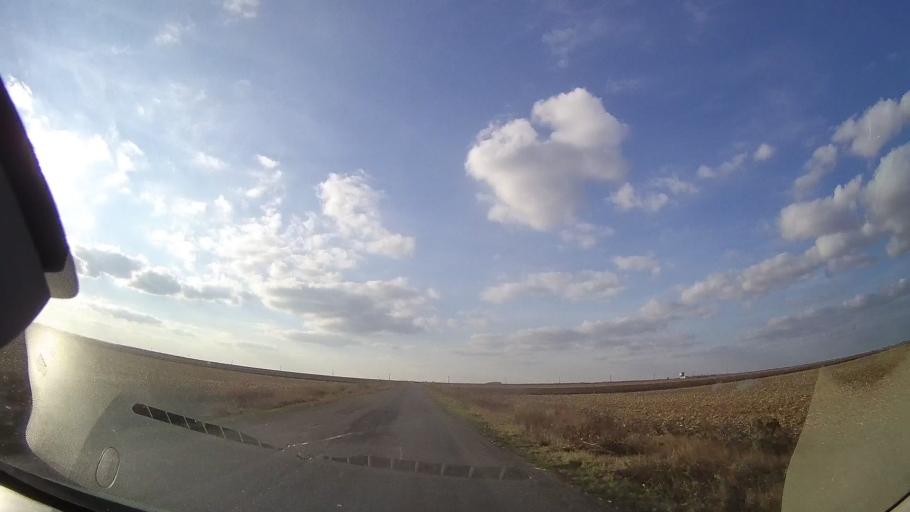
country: RO
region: Constanta
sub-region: Comuna Cerchezu
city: Cerchezu
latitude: 43.8255
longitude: 28.1308
